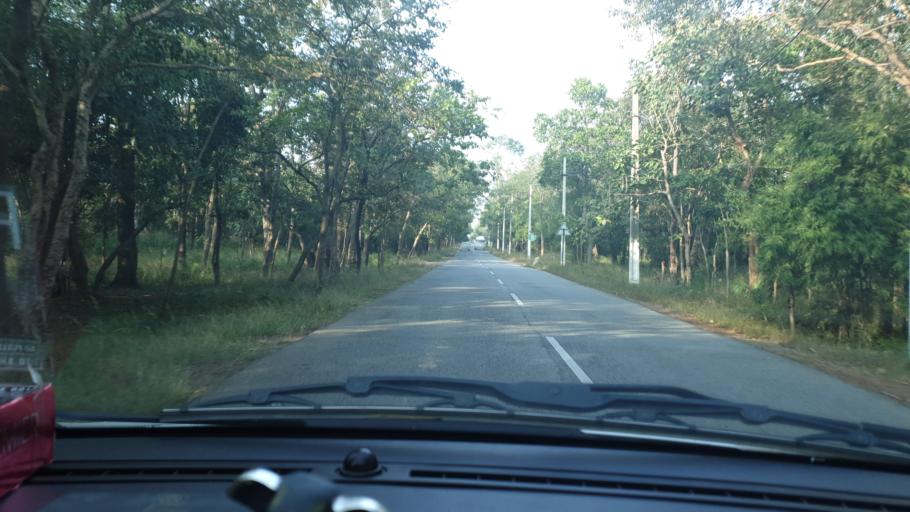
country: IN
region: Andhra Pradesh
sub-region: Kurnool
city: Srisailam
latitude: 16.2982
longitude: 78.7312
